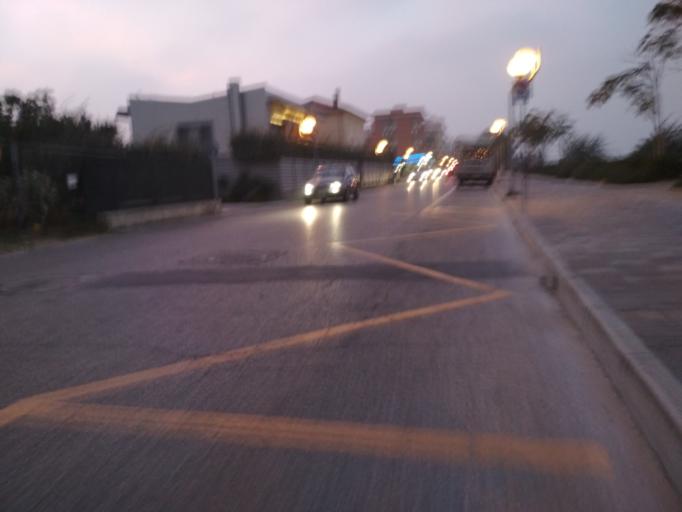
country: IT
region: Emilia-Romagna
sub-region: Provincia di Rimini
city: Rimini
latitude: 44.0813
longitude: 12.5484
